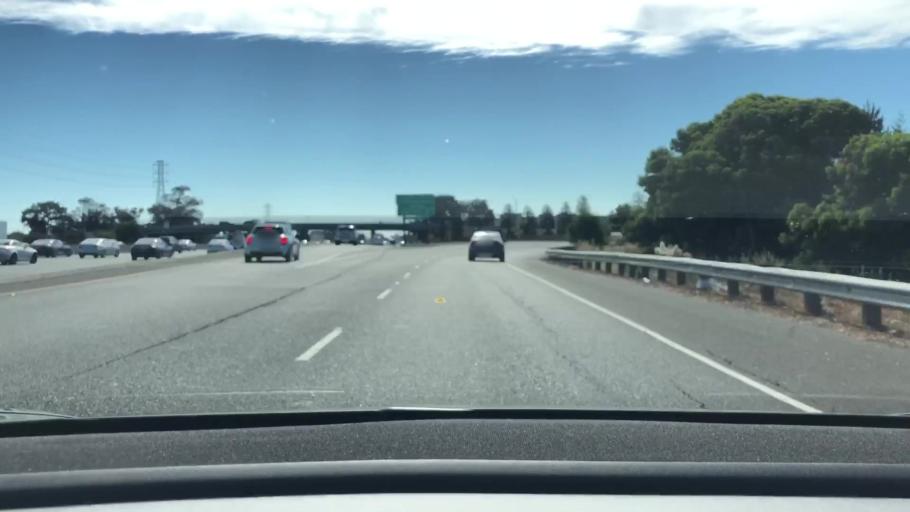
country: US
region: California
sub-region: San Mateo County
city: San Carlos
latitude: 37.5155
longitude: -122.2583
